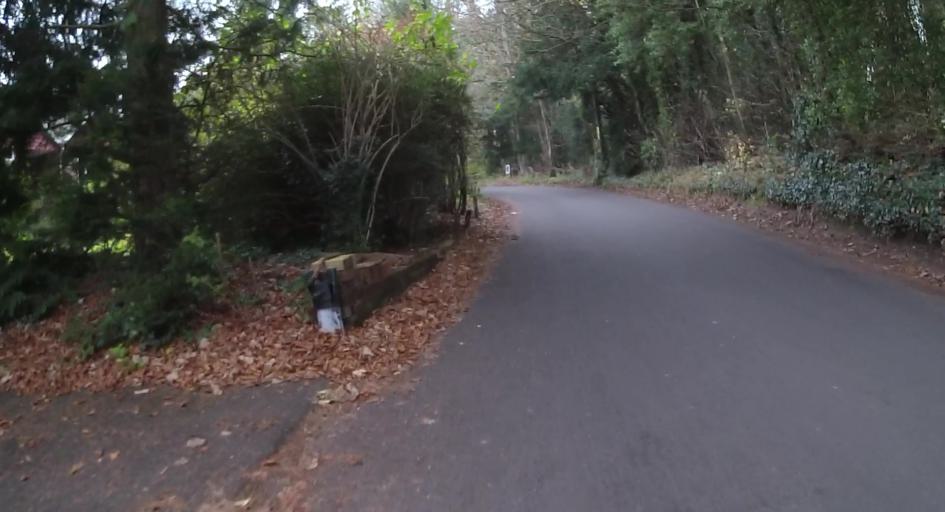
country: GB
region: England
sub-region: Hampshire
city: Kings Worthy
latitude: 51.0924
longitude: -1.2913
